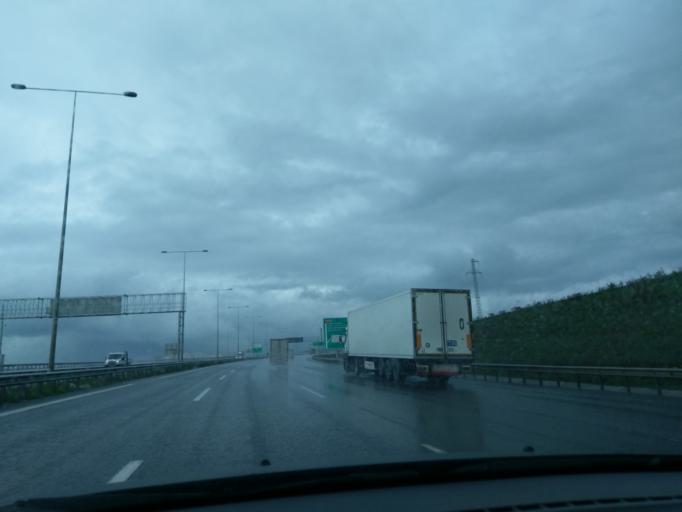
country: TR
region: Istanbul
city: Basaksehir
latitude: 41.1282
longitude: 28.8067
